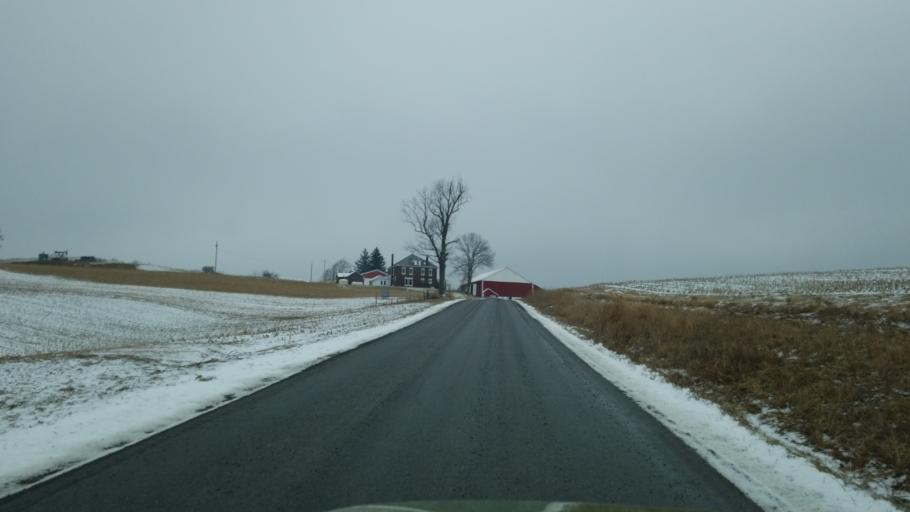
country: US
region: Pennsylvania
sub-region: Jefferson County
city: Sykesville
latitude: 41.0404
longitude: -78.7827
